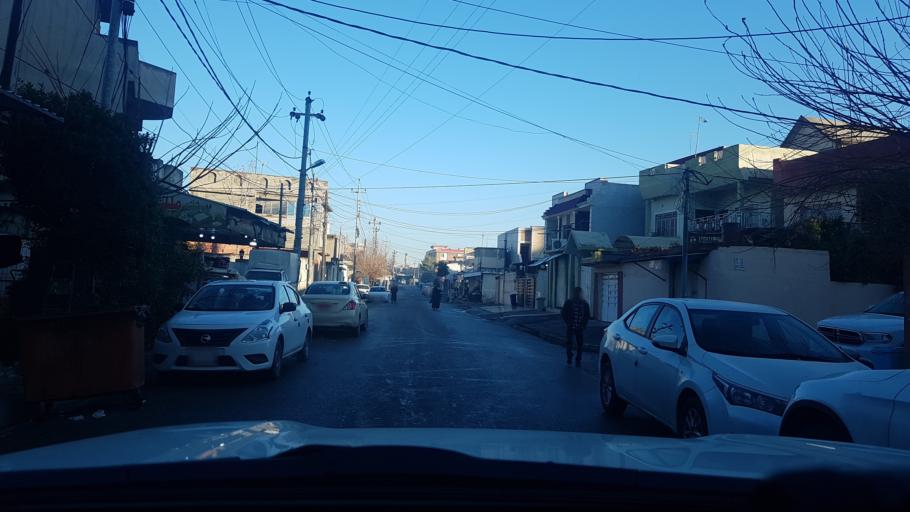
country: IQ
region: Arbil
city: Erbil
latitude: 36.2042
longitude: 44.0084
